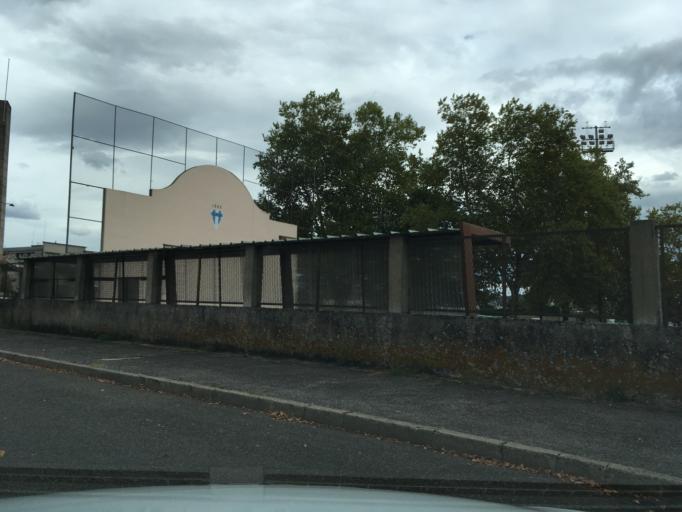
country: FR
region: Aquitaine
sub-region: Departement du Lot-et-Garonne
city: Le Passage
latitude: 44.1912
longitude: 0.6169
